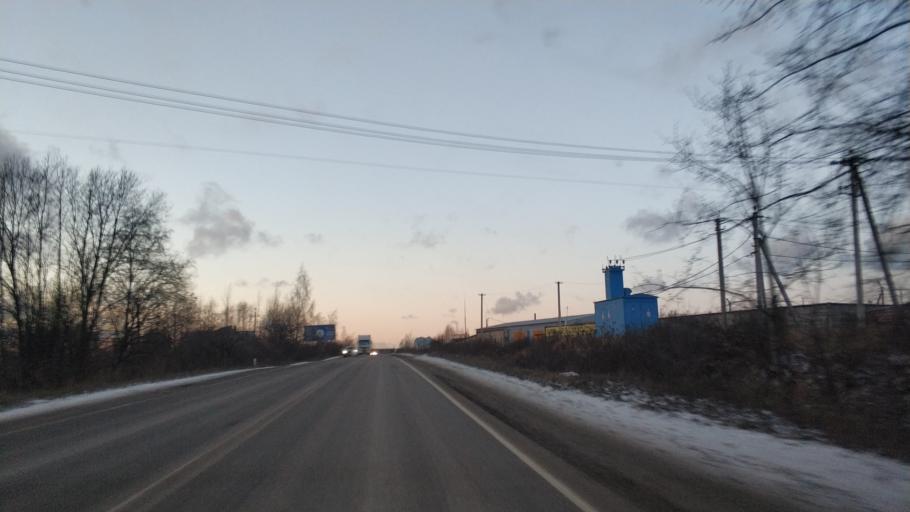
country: RU
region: St.-Petersburg
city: Pontonnyy
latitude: 59.8096
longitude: 30.6129
